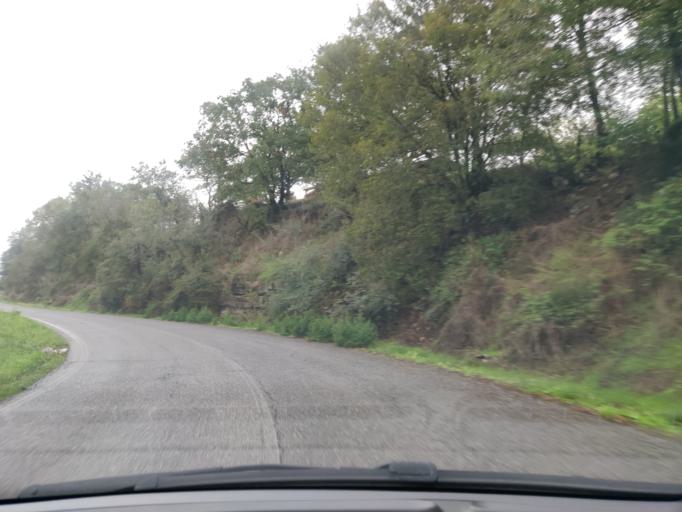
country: IT
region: Latium
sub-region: Citta metropolitana di Roma Capitale
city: Allumiere
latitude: 42.1442
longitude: 11.8831
